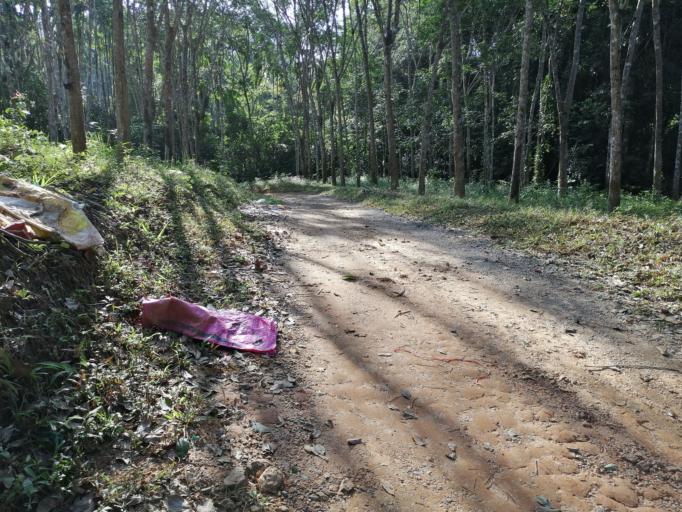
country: TH
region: Phatthalung
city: Pa Phayom
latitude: 7.9371
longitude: 99.8004
